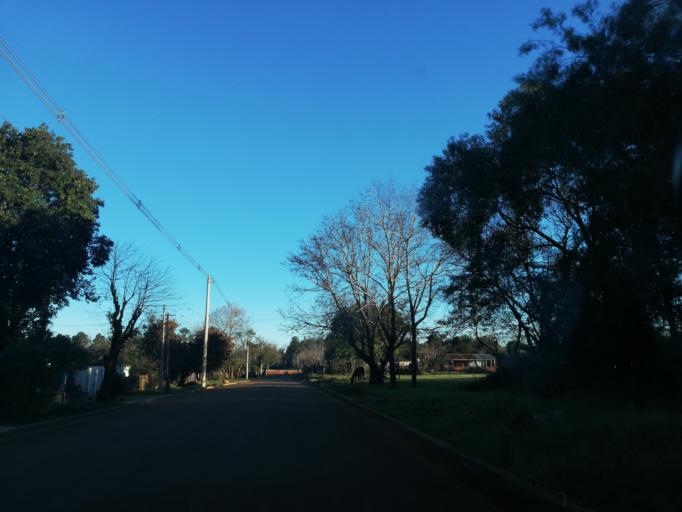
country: AR
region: Misiones
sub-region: Departamento de Candelaria
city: Candelaria
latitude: -27.4683
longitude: -55.7494
